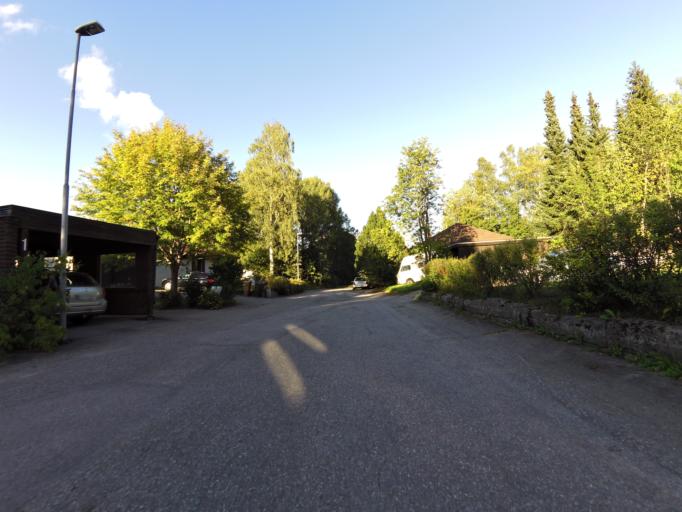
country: SE
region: Gaevleborg
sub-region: Gavle Kommun
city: Gavle
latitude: 60.7101
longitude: 17.1478
